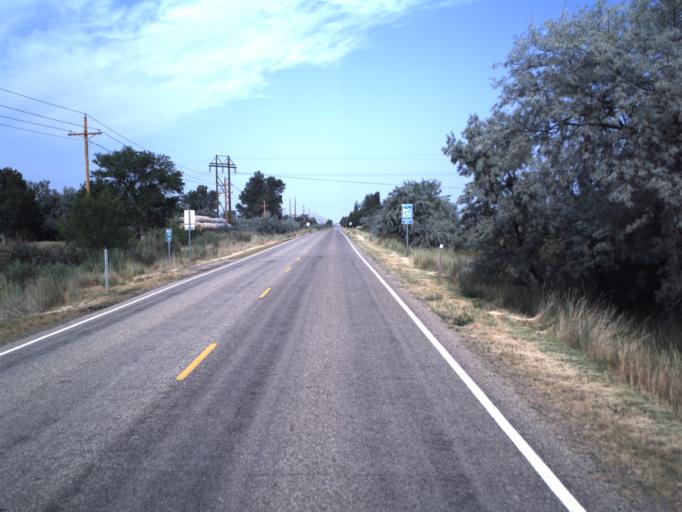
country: US
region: Utah
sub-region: Duchesne County
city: Roosevelt
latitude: 40.2581
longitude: -110.1382
